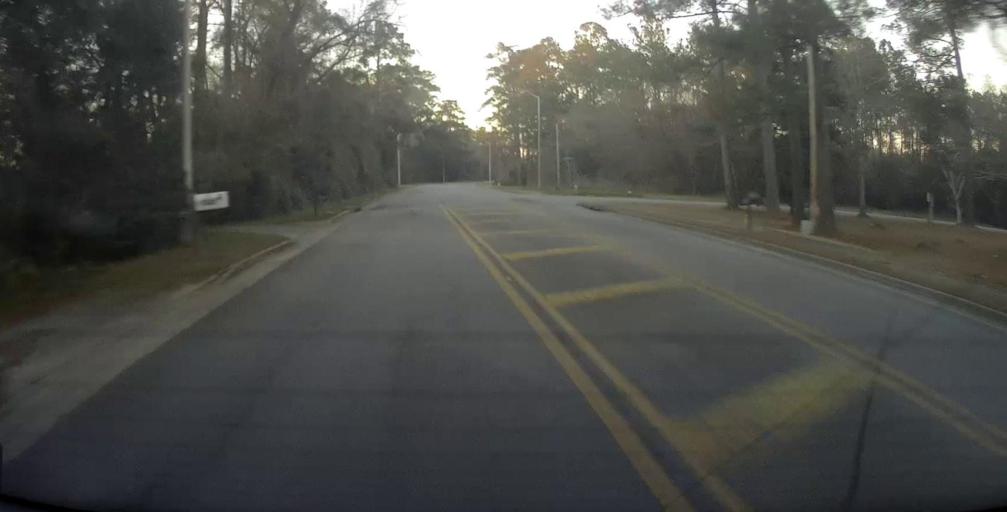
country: US
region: Georgia
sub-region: Dougherty County
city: Albany
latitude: 31.5328
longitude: -84.1370
